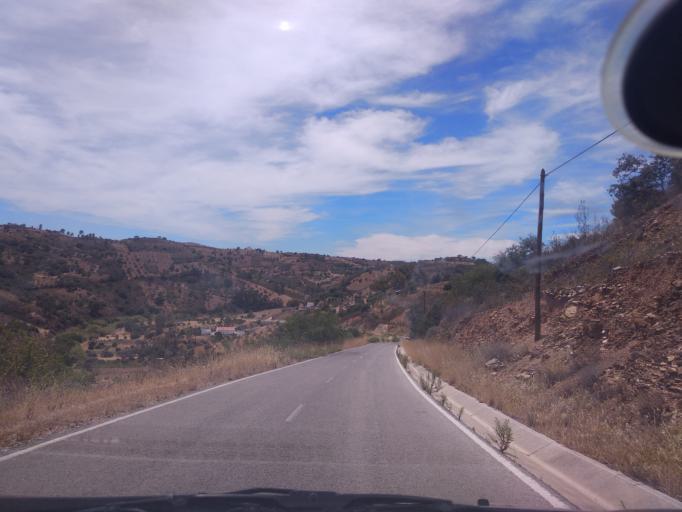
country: PT
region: Faro
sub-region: Sao Bras de Alportel
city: Sao Bras de Alportel
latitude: 37.1832
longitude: -7.7983
